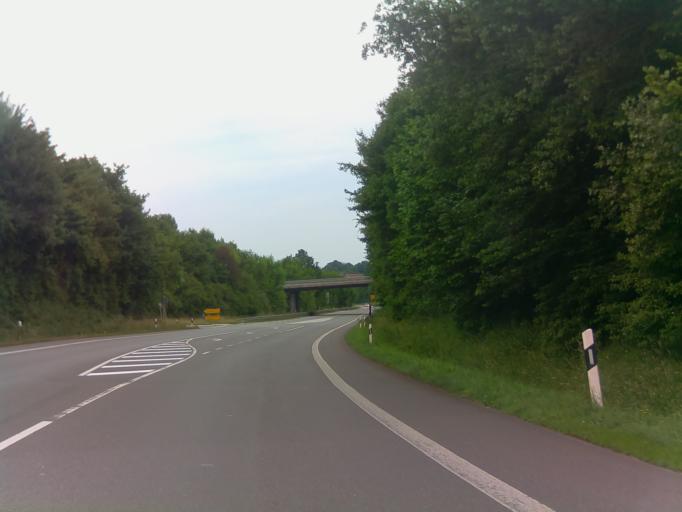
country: DE
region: North Rhine-Westphalia
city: Warburg
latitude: 51.5917
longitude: 9.1338
